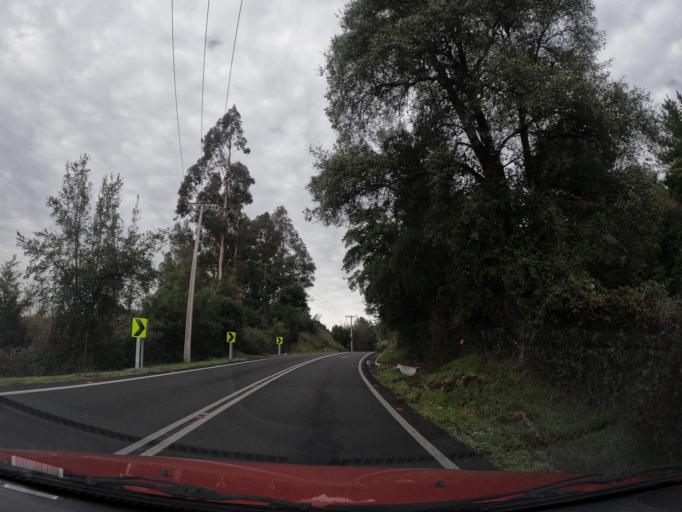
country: CL
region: Maule
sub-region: Provincia de Linares
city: Linares
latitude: -35.9118
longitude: -71.4821
